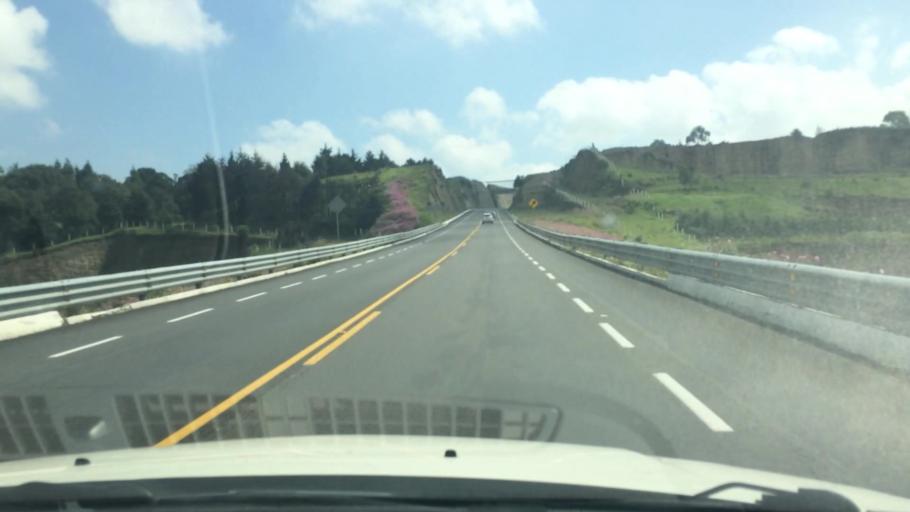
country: MX
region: Mexico
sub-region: Almoloya de Juarez
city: San Pedro de la Hortaliza (Ejido Almoloyan)
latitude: 19.3777
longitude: -99.8648
